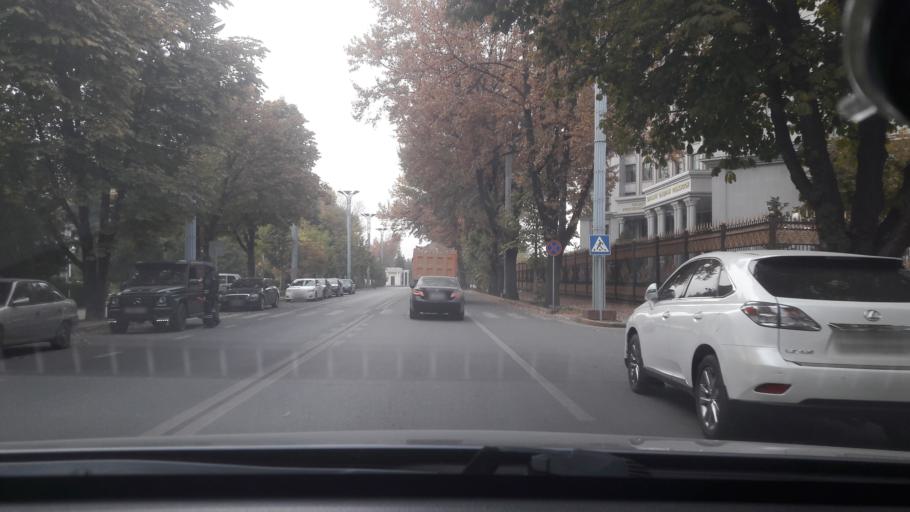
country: TJ
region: Dushanbe
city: Dushanbe
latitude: 38.5784
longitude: 68.7842
